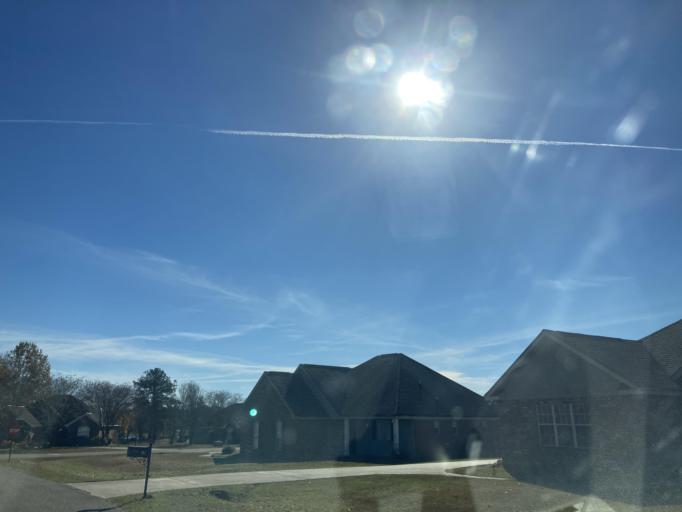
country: US
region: Mississippi
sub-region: Forrest County
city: Petal
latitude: 31.3204
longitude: -89.1863
